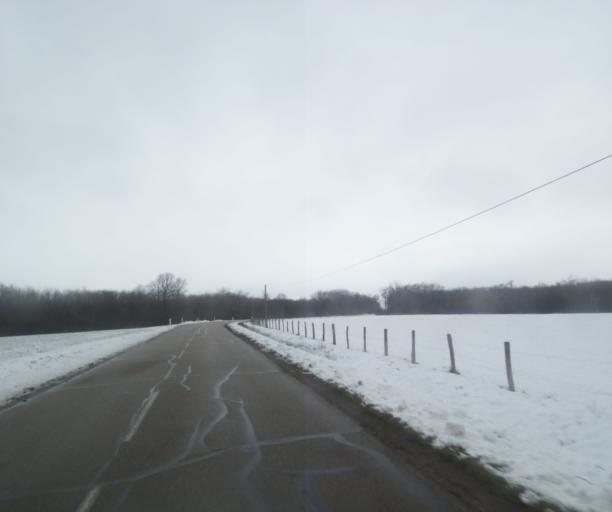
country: FR
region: Champagne-Ardenne
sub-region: Departement de la Haute-Marne
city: Laneuville-a-Remy
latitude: 48.4307
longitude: 4.8535
